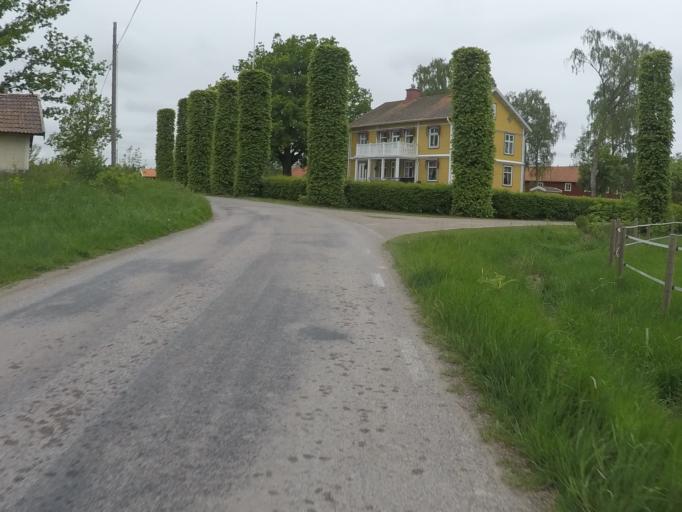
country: SE
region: Vaestmanland
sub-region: Hallstahammars Kommun
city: Kolback
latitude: 59.5479
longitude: 16.3056
